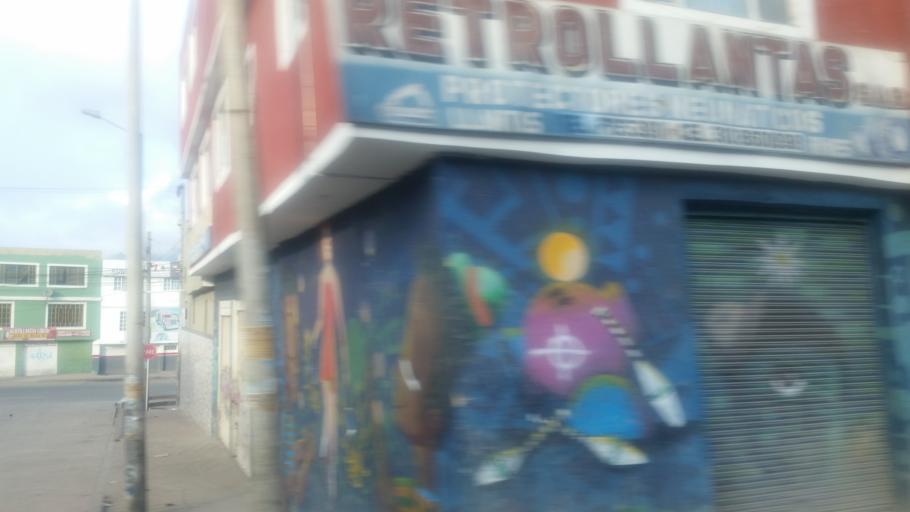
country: CO
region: Bogota D.C.
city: Bogota
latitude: 4.5602
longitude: -74.1389
